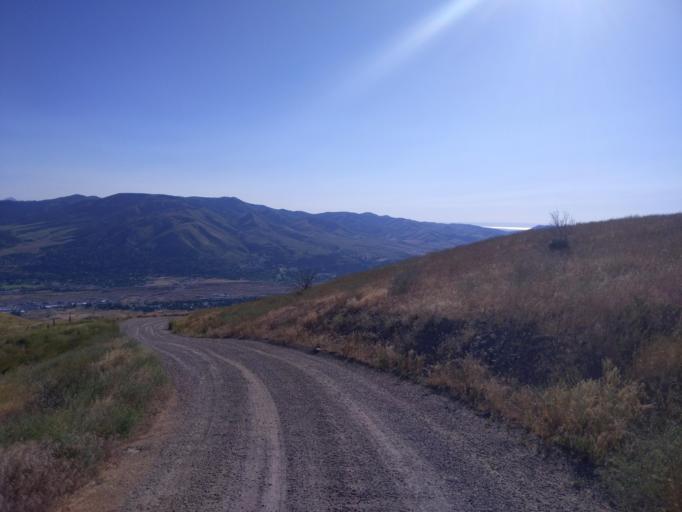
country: US
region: Idaho
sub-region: Bannock County
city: Pocatello
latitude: 42.8478
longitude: -112.3678
